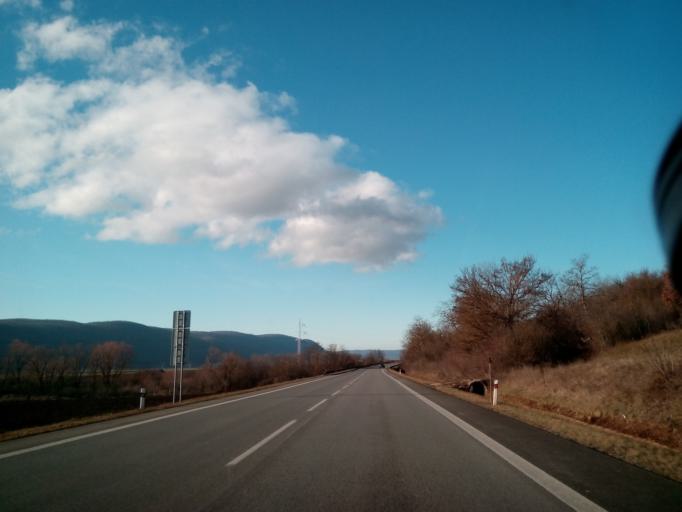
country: SK
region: Kosicky
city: Medzev
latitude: 48.5993
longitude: 20.8124
